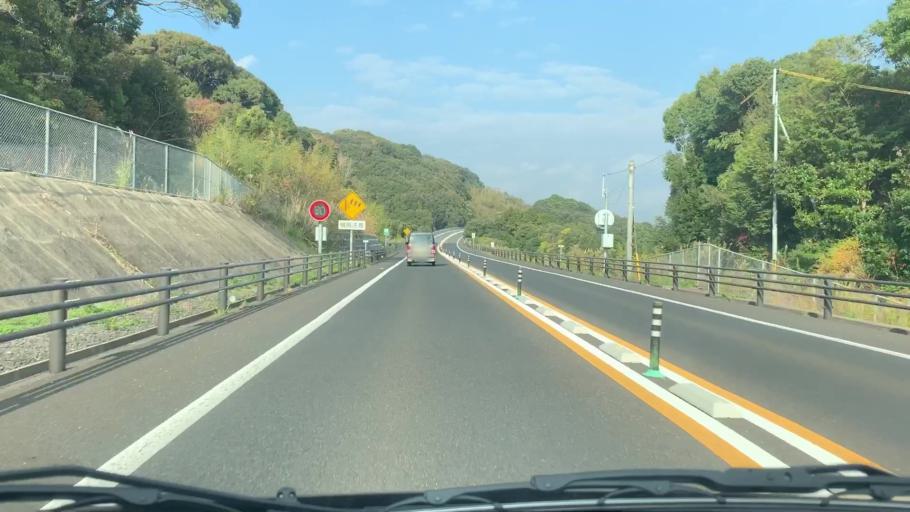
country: JP
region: Nagasaki
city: Sasebo
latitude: 33.0286
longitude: 129.7381
